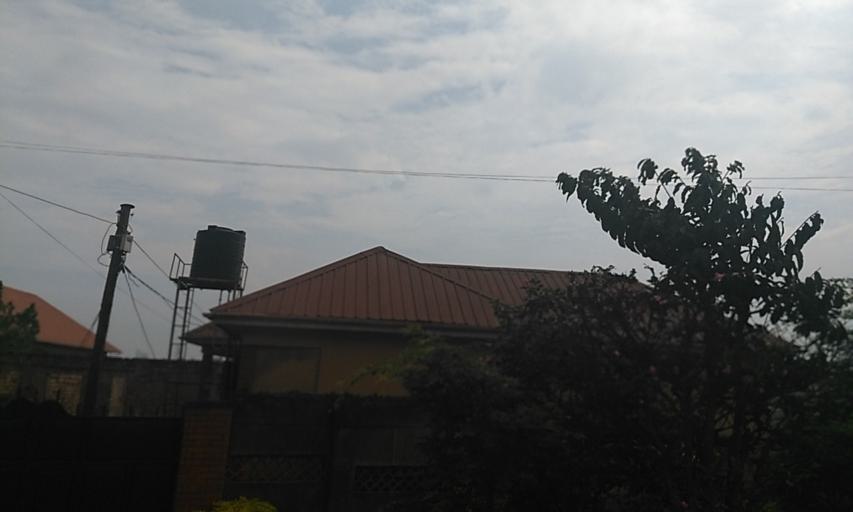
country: UG
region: Central Region
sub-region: Kampala District
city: Kampala
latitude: 0.3009
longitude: 32.5591
